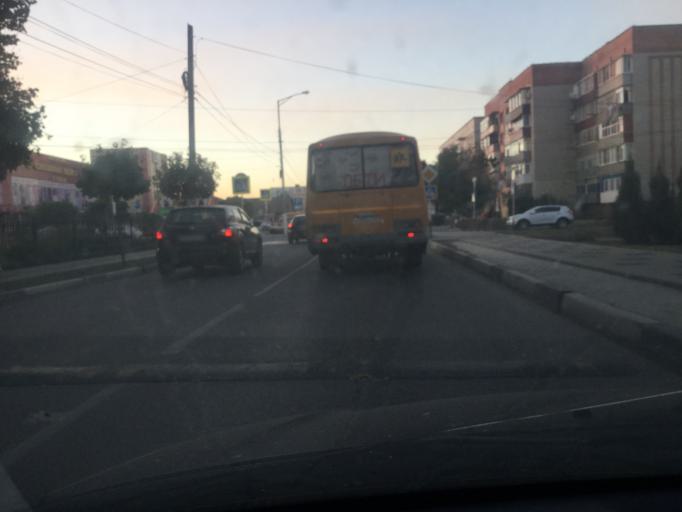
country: RU
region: Krasnodarskiy
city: Slavyansk-na-Kubani
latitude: 45.2540
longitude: 38.1132
